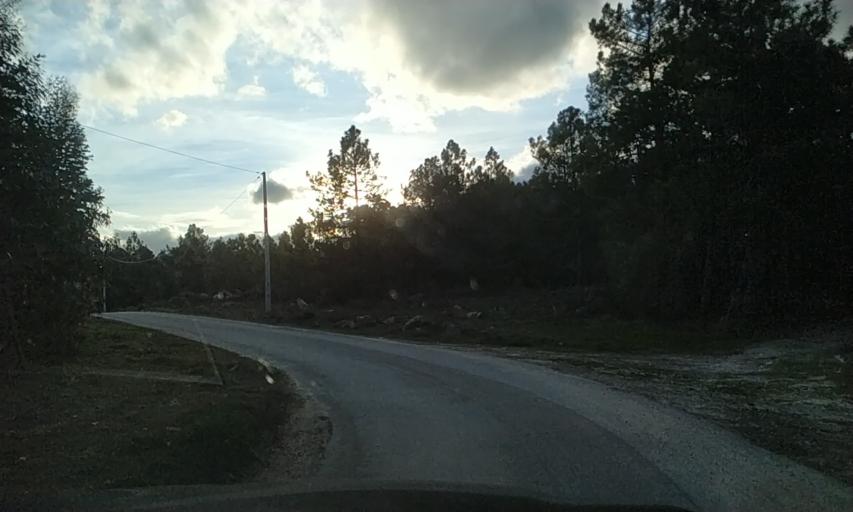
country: PT
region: Braganca
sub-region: Carrazeda de Ansiaes
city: Carrazeda de Anciaes
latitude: 41.2218
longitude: -7.3588
